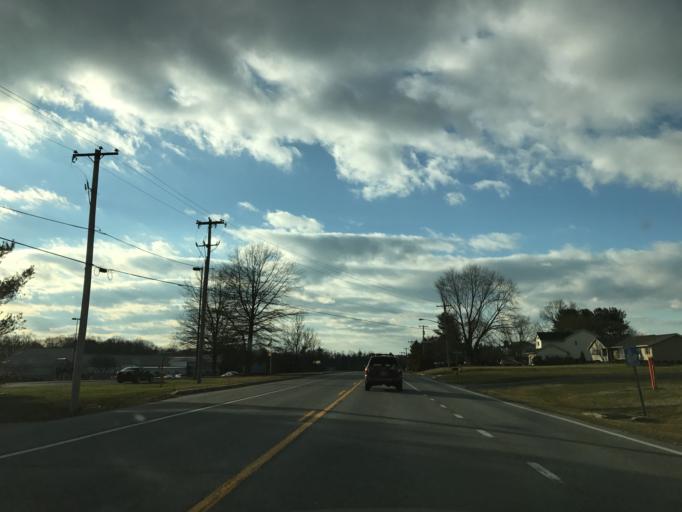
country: US
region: Maryland
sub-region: Cecil County
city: Rising Sun
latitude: 39.6925
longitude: -76.0552
